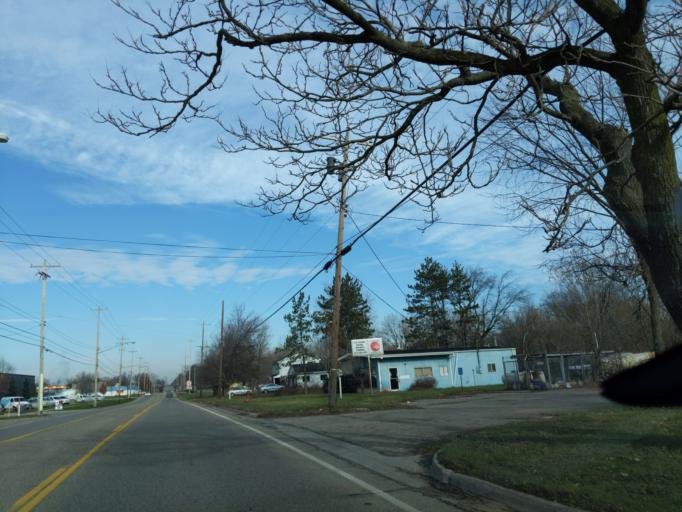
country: US
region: Michigan
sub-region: Ingham County
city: Holt
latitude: 42.6765
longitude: -84.5235
